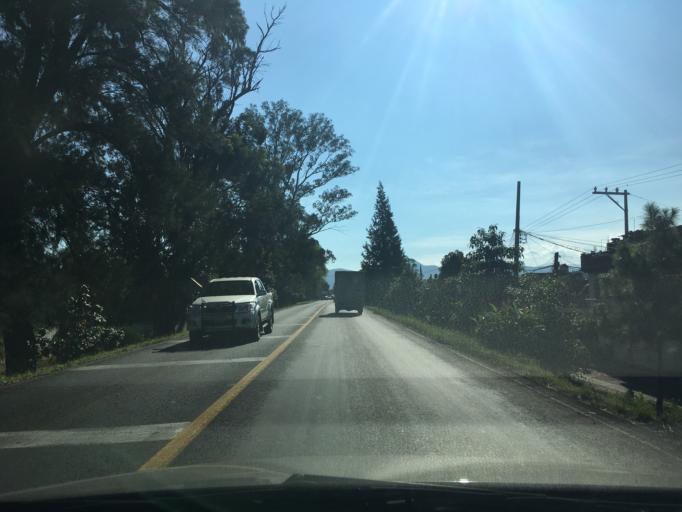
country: MX
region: Mexico
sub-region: Chalco
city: Chilchota
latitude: 19.8505
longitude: -102.1188
